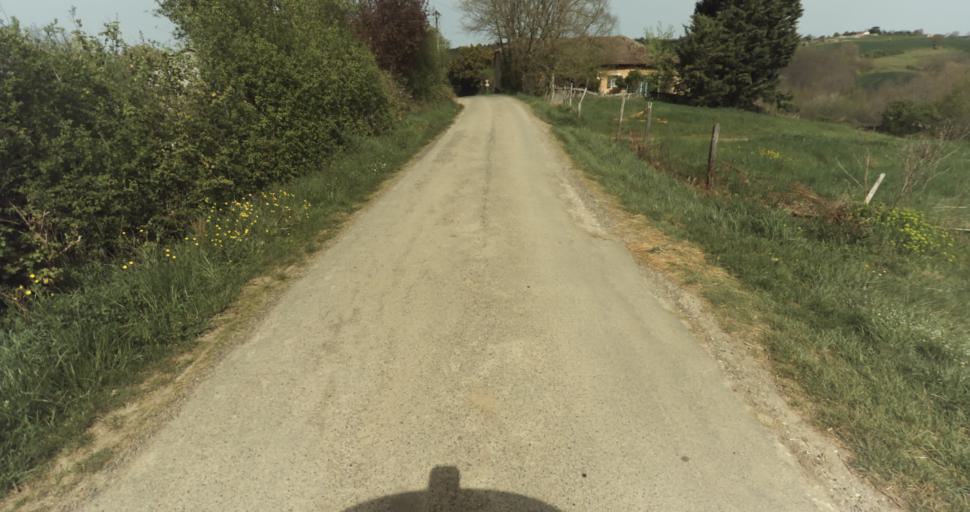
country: FR
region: Midi-Pyrenees
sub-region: Departement du Tarn-et-Garonne
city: Moissac
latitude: 44.1304
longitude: 1.1100
